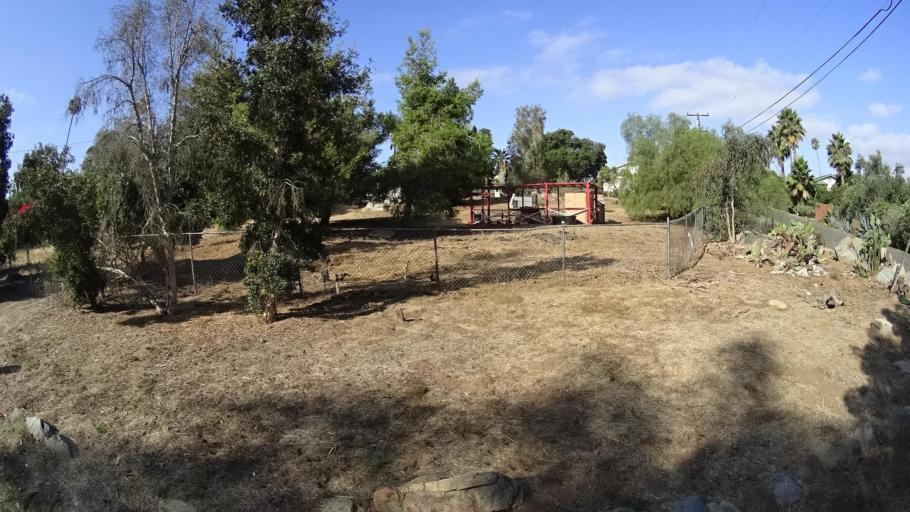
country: US
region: California
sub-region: San Diego County
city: Vista
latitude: 33.1766
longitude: -117.2358
